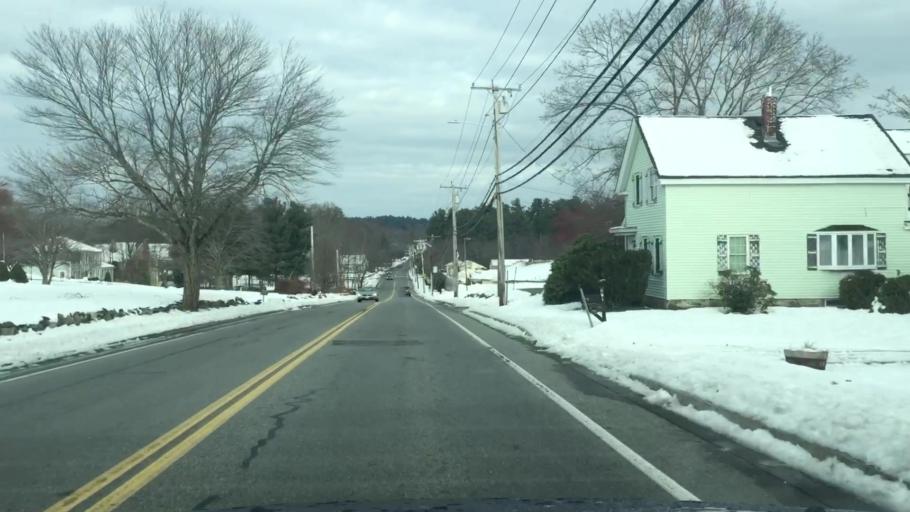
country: US
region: Massachusetts
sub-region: Middlesex County
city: Dracut
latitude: 42.6717
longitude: -71.3510
